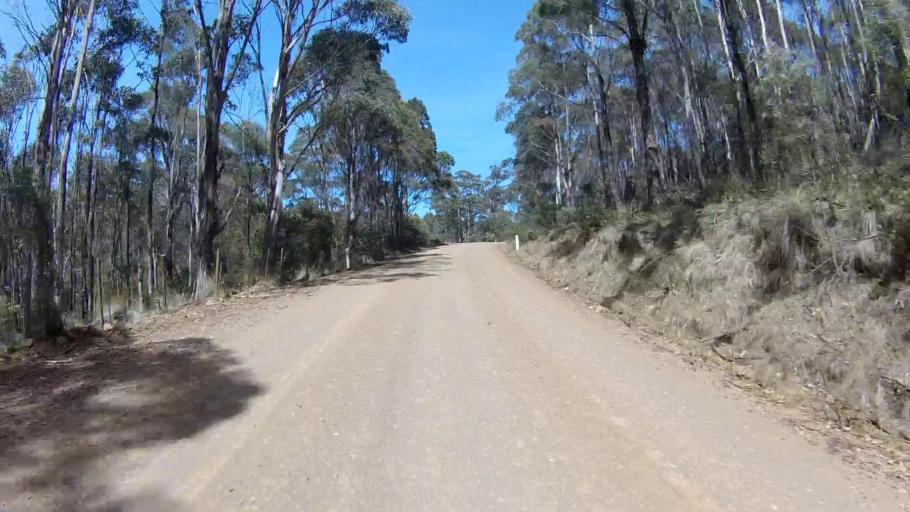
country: AU
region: Tasmania
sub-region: Sorell
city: Sorell
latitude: -42.6544
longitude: 147.7407
